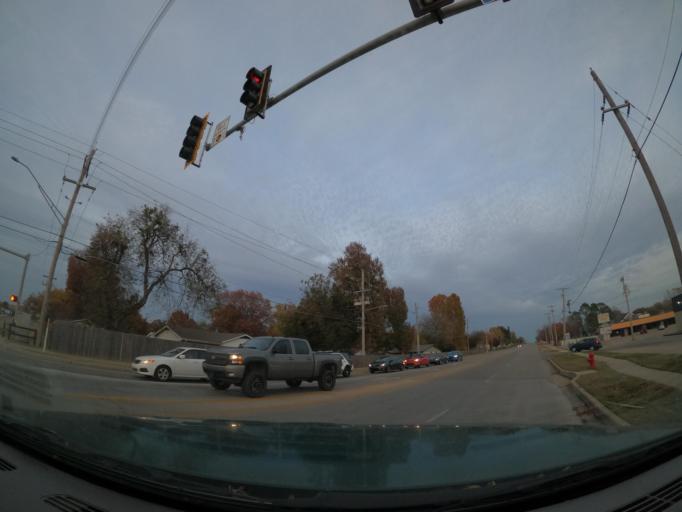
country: US
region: Oklahoma
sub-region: Tulsa County
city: Broken Arrow
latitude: 36.0318
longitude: -95.7972
